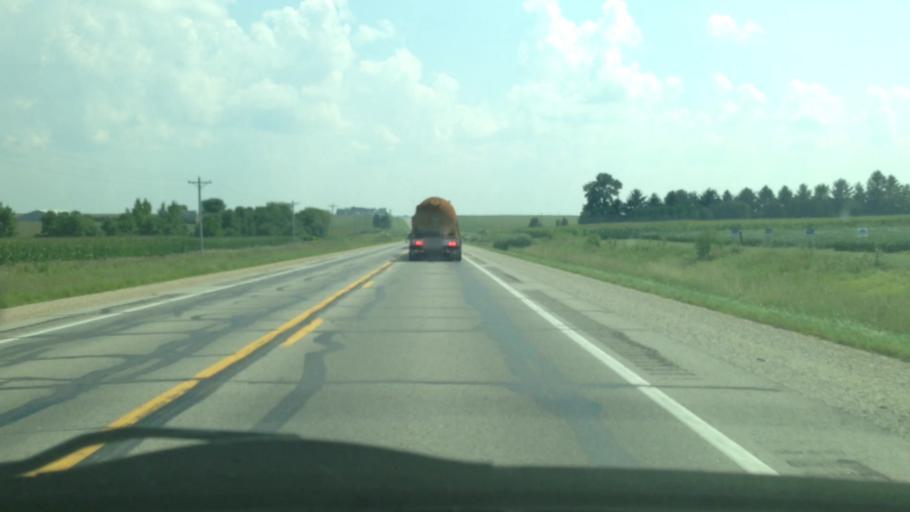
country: US
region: Iowa
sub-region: Chickasaw County
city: New Hampton
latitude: 43.1465
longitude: -92.2989
